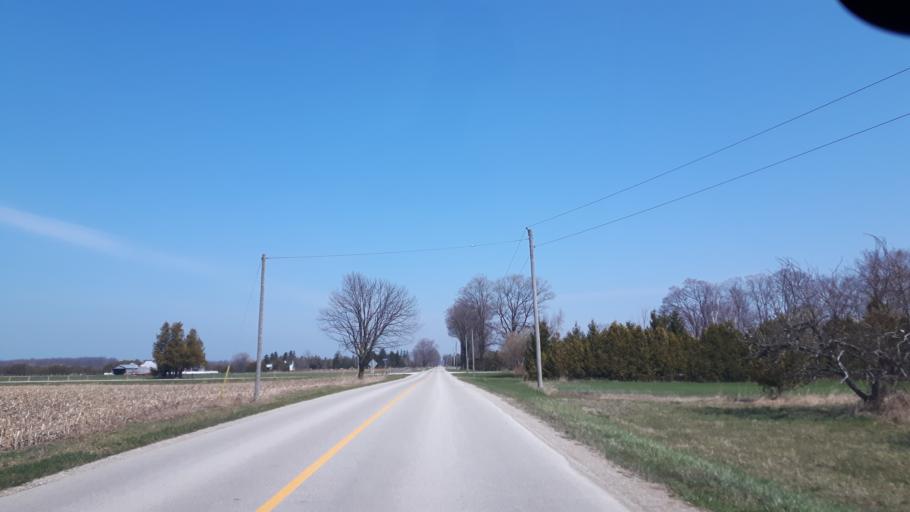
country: CA
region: Ontario
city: Goderich
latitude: 43.6599
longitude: -81.6846
